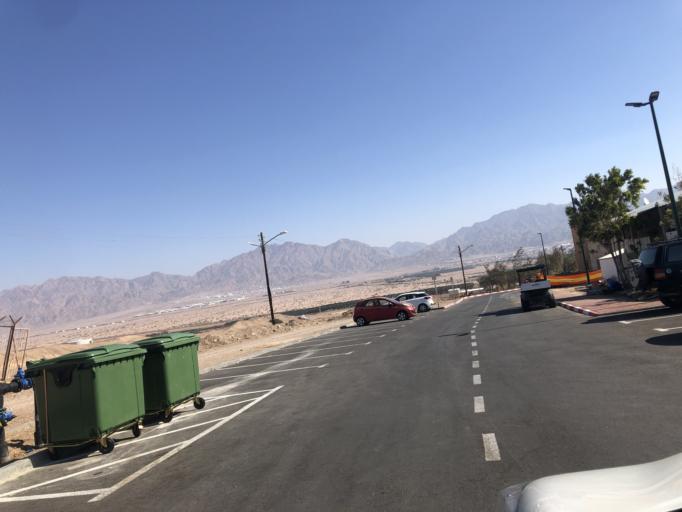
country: IL
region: Southern District
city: Eilat
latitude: 29.5834
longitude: 34.9618
